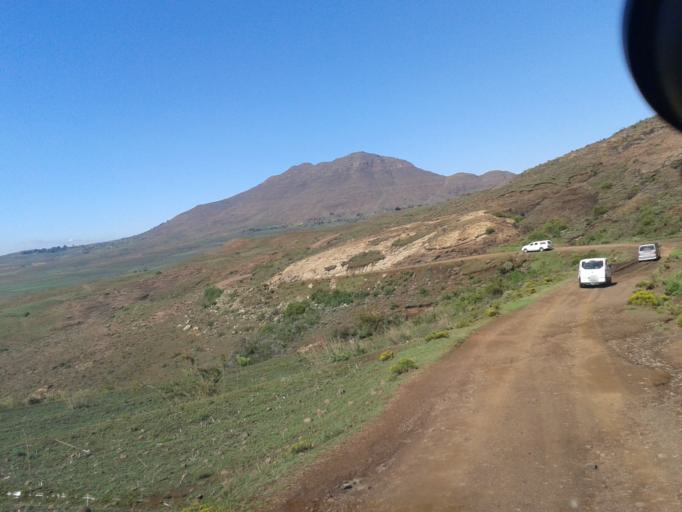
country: LS
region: Maseru
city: Nako
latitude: -29.8392
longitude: 27.5685
